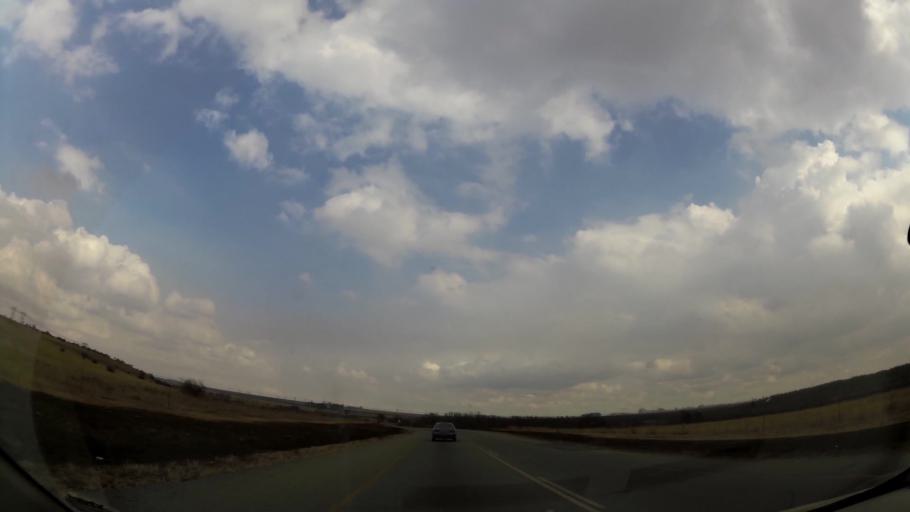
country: ZA
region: Orange Free State
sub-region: Fezile Dabi District Municipality
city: Sasolburg
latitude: -26.8001
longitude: 27.9139
